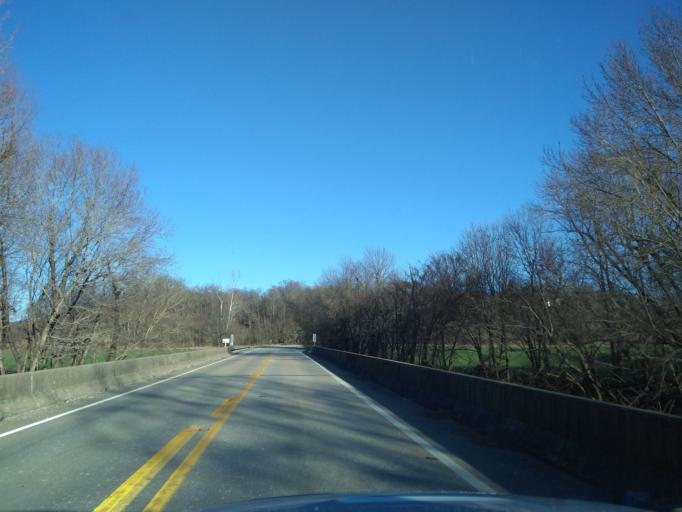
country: US
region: Arkansas
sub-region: Washington County
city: Farmington
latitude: 36.1030
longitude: -94.3443
